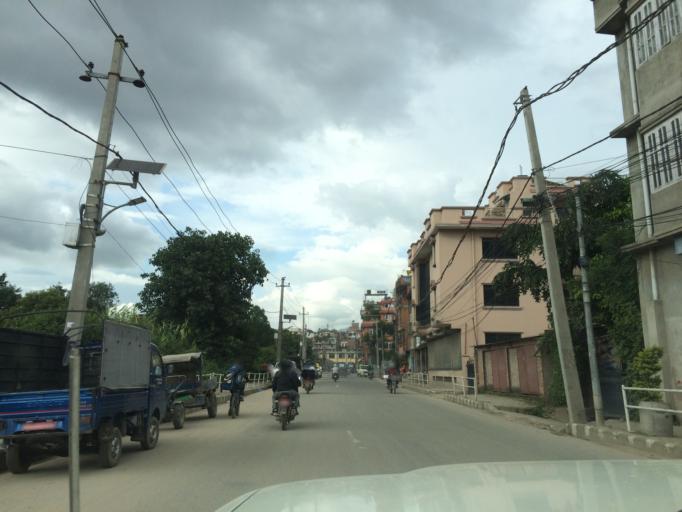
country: NP
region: Central Region
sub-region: Bagmati Zone
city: Kathmandu
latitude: 27.6947
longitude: 85.3033
